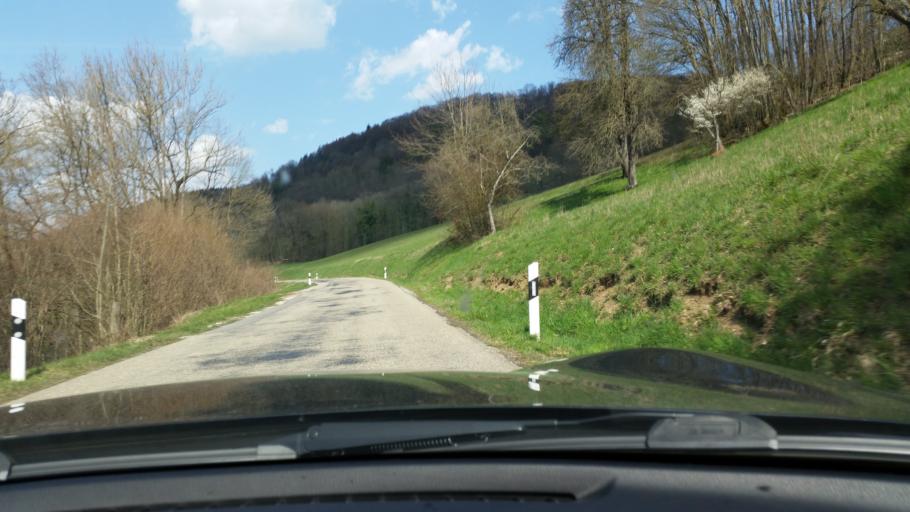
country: DE
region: Baden-Wuerttemberg
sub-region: Regierungsbezirk Stuttgart
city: Langenburg
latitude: 49.2607
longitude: 9.8433
